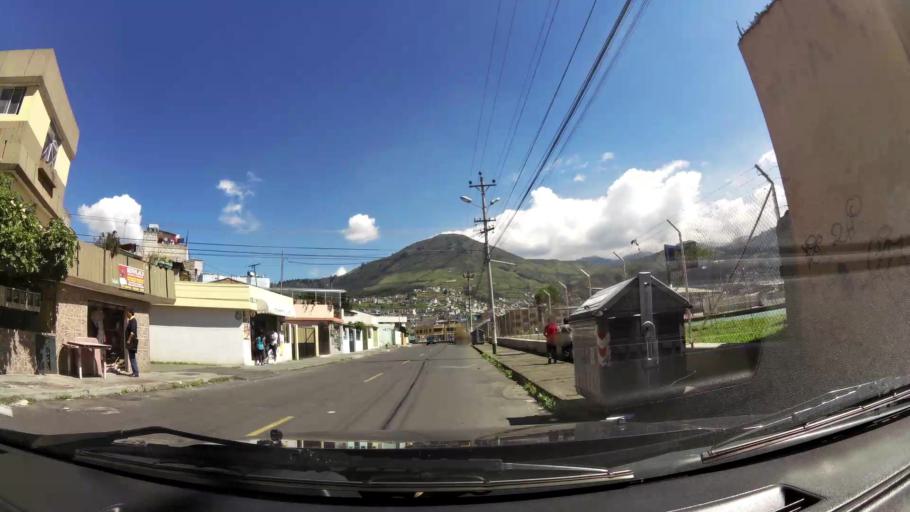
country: EC
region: Pichincha
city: Quito
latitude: -0.2554
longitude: -78.5365
